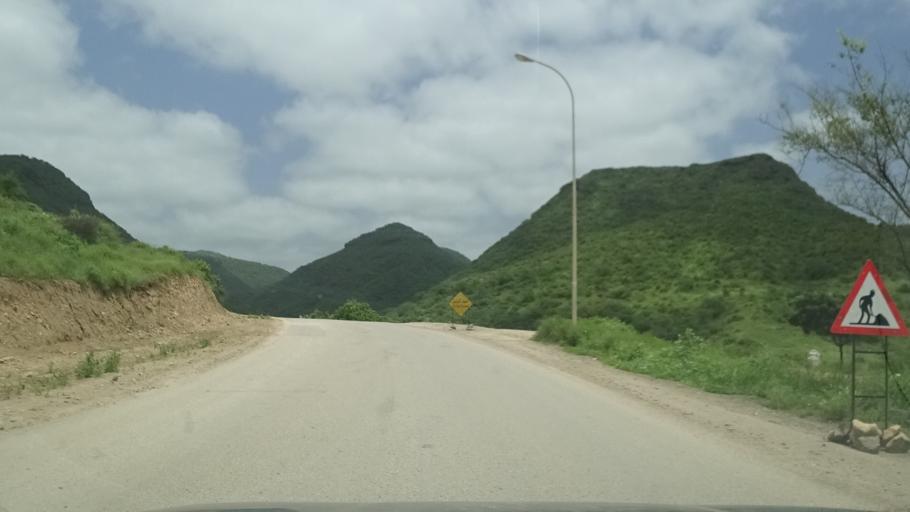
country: OM
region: Zufar
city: Salalah
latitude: 17.1492
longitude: 54.1769
